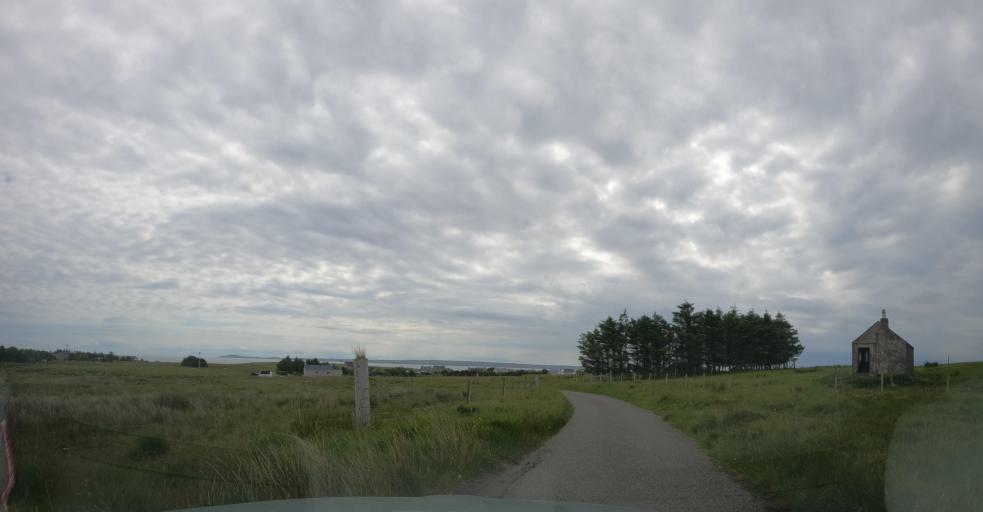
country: GB
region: Scotland
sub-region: Eilean Siar
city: Isle of Lewis
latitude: 58.2728
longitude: -6.3009
